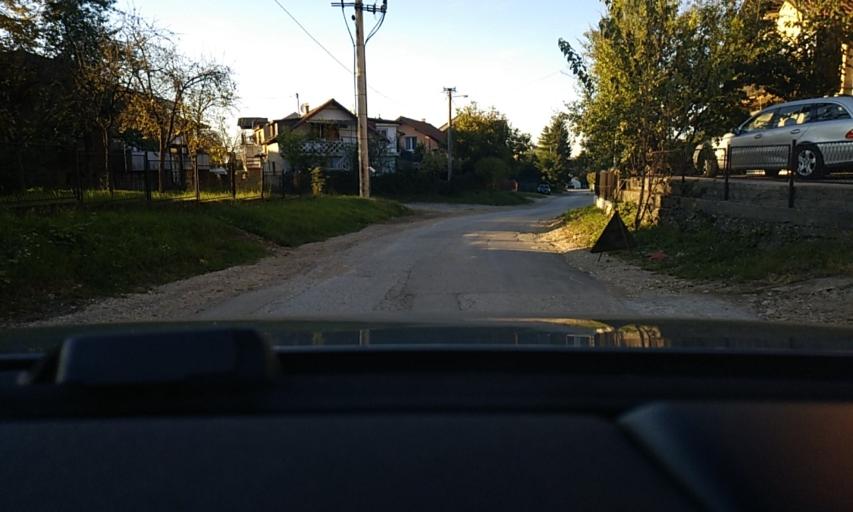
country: BA
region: Republika Srpska
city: Mejdan - Obilicevo
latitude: 44.7559
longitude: 17.1911
